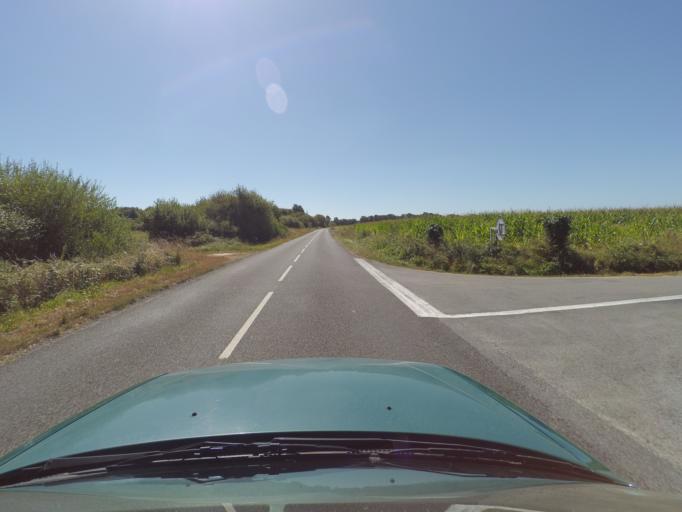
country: FR
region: Pays de la Loire
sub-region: Departement de la Loire-Atlantique
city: Le Bignon
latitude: 47.1075
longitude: -1.4970
